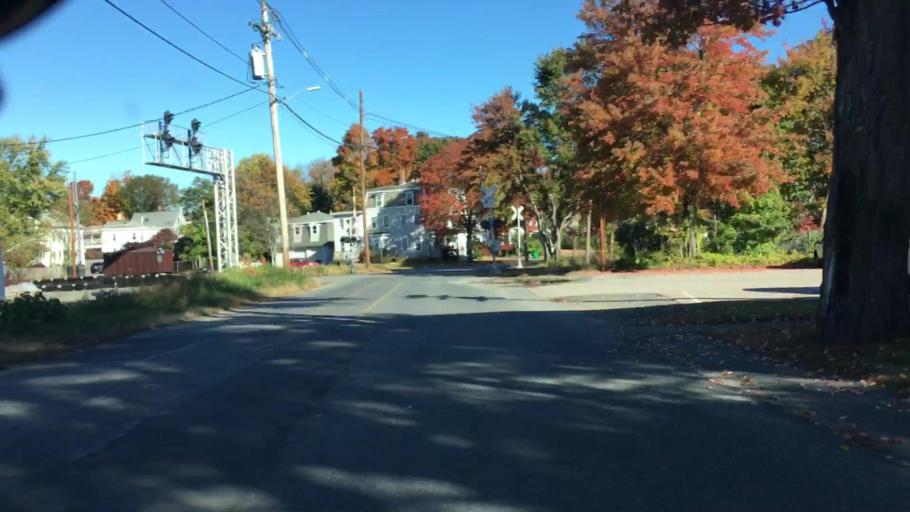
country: US
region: Massachusetts
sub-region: Middlesex County
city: Ashland
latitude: 42.2599
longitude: -71.4677
